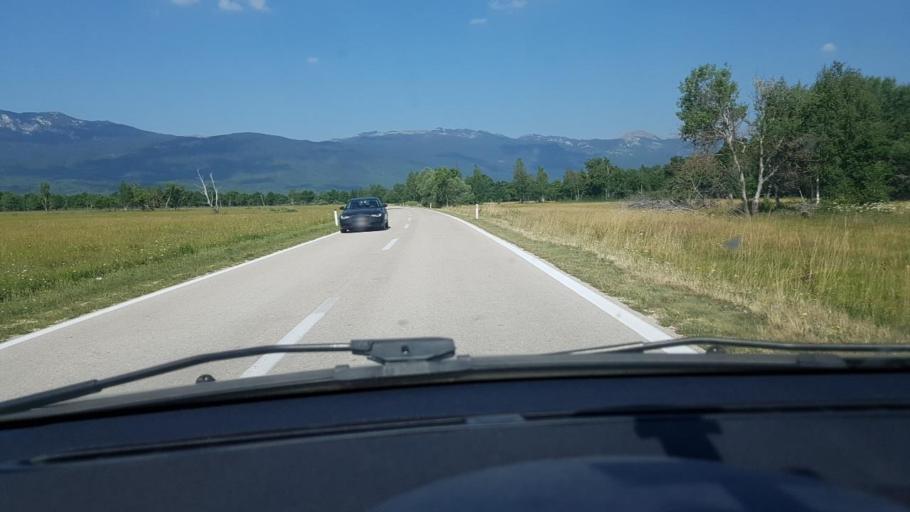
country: BA
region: Federation of Bosnia and Herzegovina
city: Glamoc
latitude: 43.9844
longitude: 16.6892
